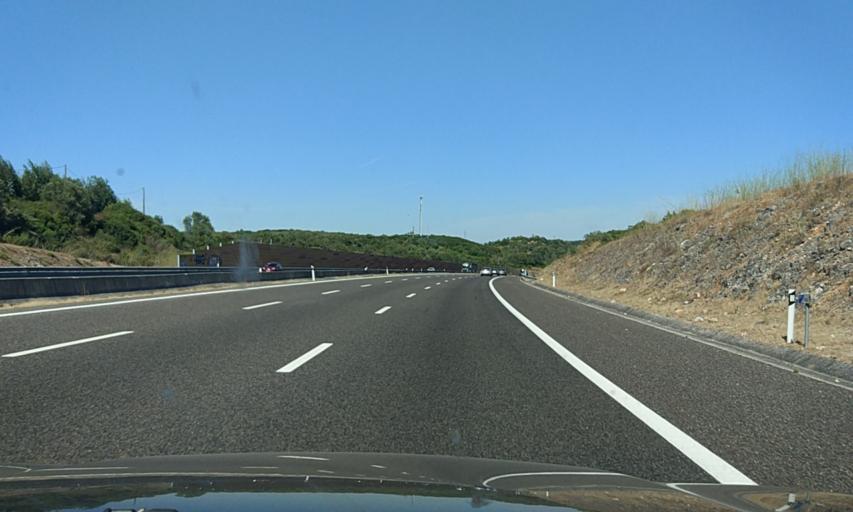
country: PT
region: Santarem
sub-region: Santarem
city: Santarem
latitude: 39.2334
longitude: -8.7597
